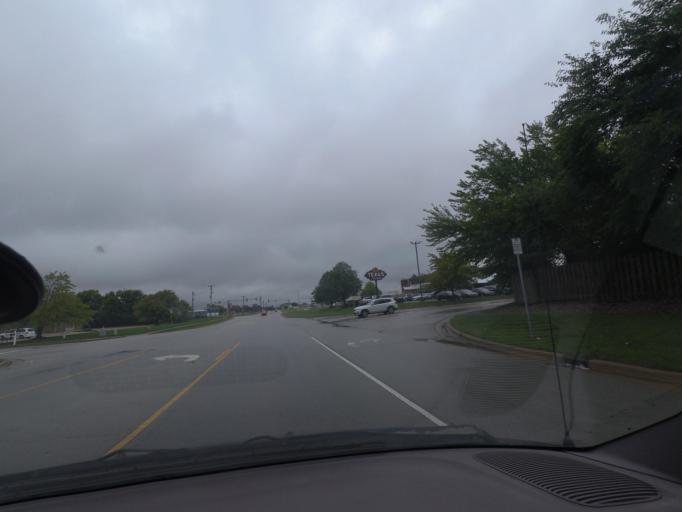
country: US
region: Illinois
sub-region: Champaign County
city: Champaign
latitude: 40.1171
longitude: -88.2817
